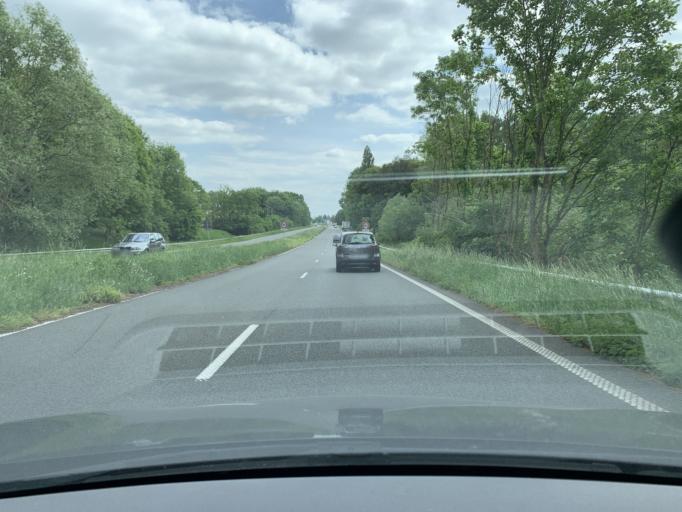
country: FR
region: Nord-Pas-de-Calais
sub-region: Departement du Nord
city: Lauwin-Planque
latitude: 50.3896
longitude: 3.0478
